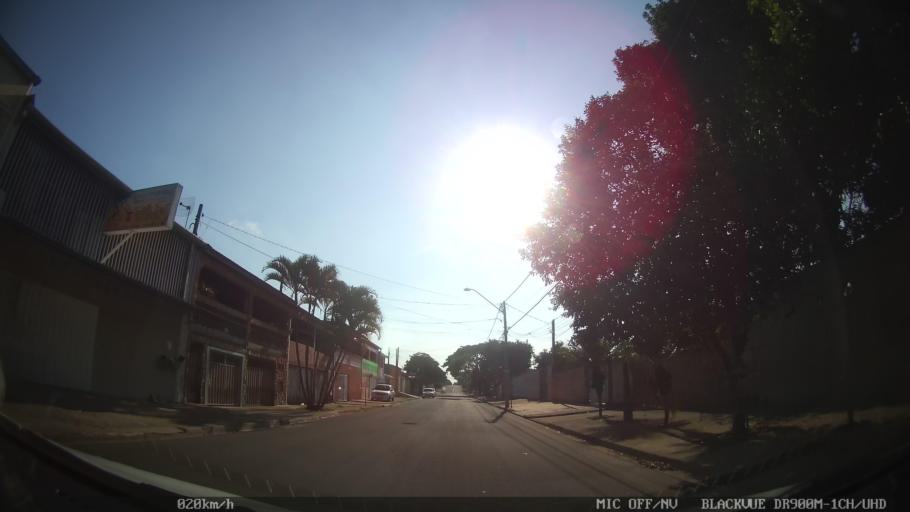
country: BR
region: Sao Paulo
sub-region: Indaiatuba
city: Indaiatuba
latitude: -22.9988
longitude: -47.1375
